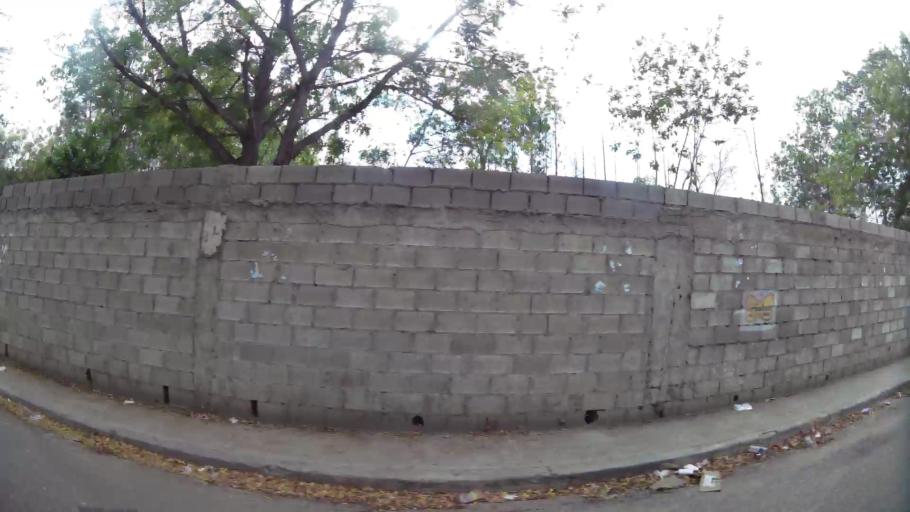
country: DO
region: Santiago
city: Santiago de los Caballeros
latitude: 19.4269
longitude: -70.6835
